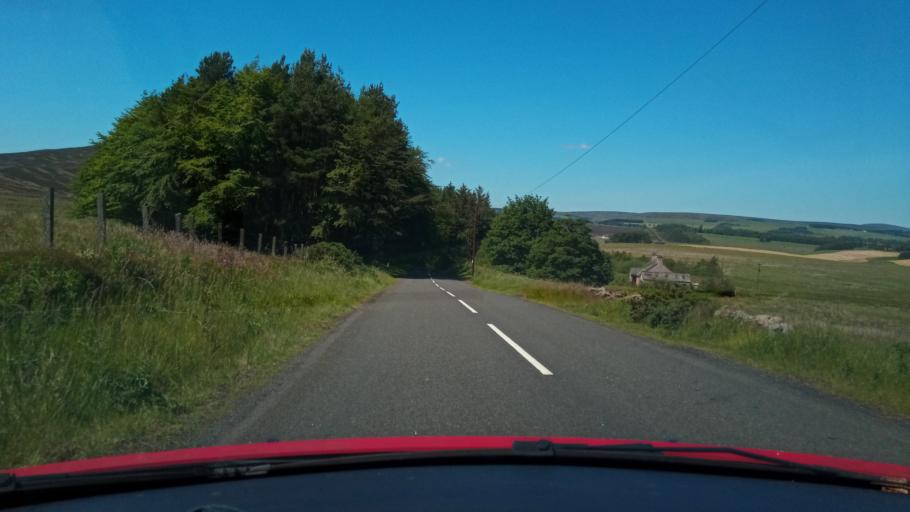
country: GB
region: Scotland
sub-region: The Scottish Borders
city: Duns
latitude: 55.7849
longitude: -2.4518
